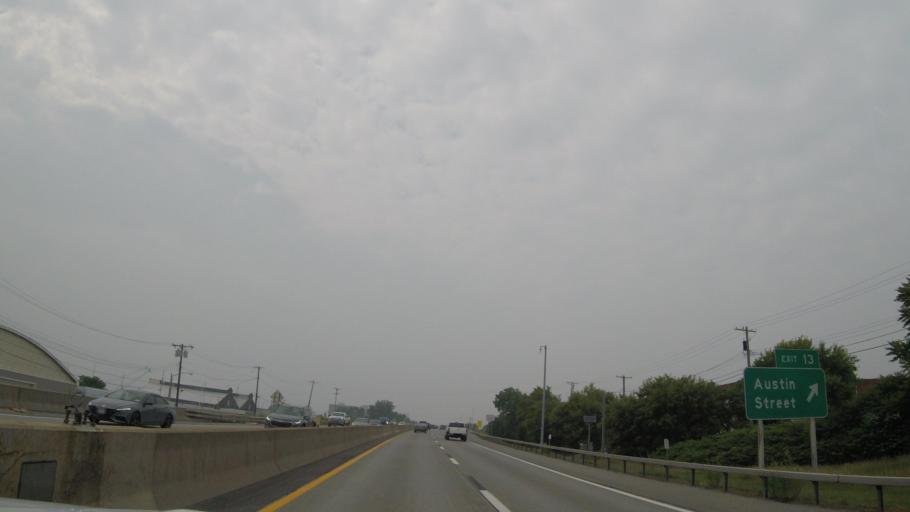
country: CA
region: Ontario
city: Fort Erie
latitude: 42.9345
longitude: -78.9034
